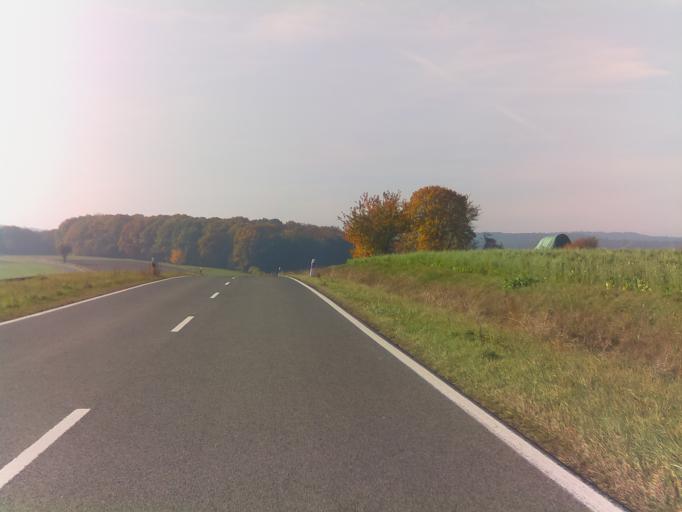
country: DE
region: Bavaria
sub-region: Regierungsbezirk Unterfranken
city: Eltmann
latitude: 49.9680
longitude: 10.6510
